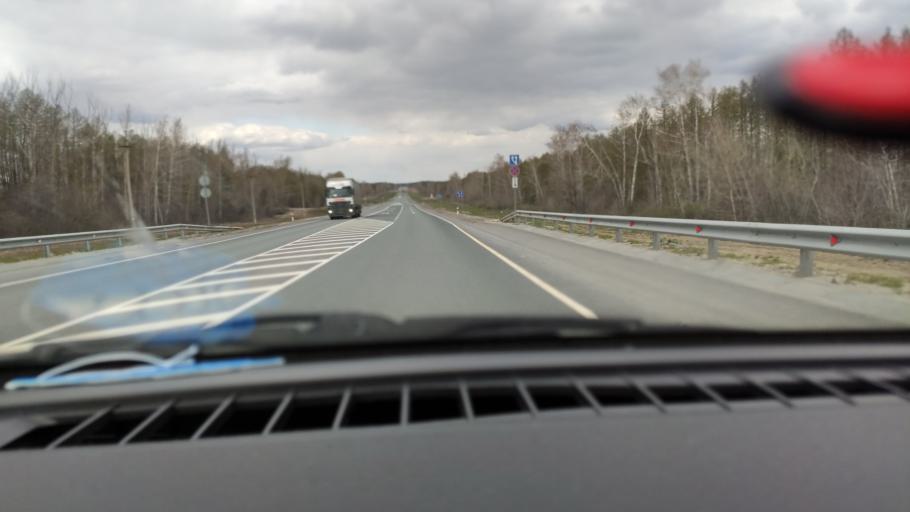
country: RU
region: Saratov
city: Shikhany
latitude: 52.1527
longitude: 47.1841
